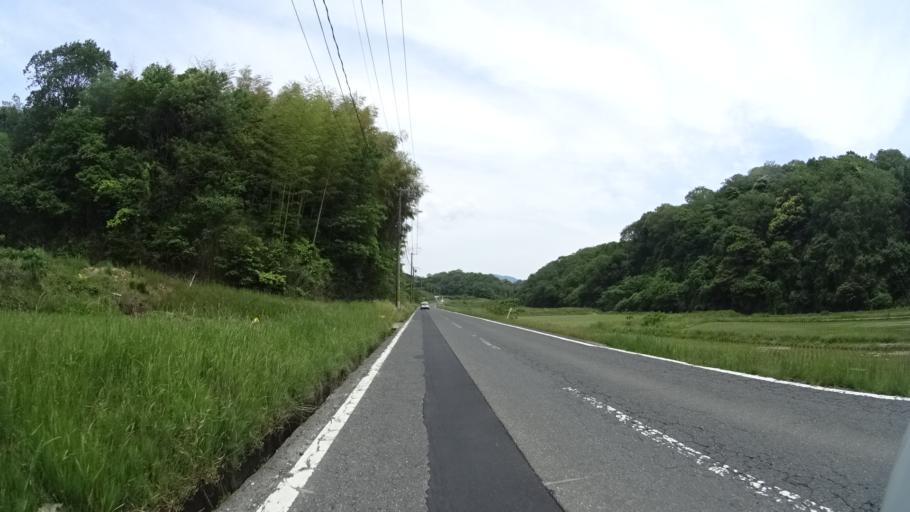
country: JP
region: Kyoto
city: Miyazu
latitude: 35.6841
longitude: 135.0618
